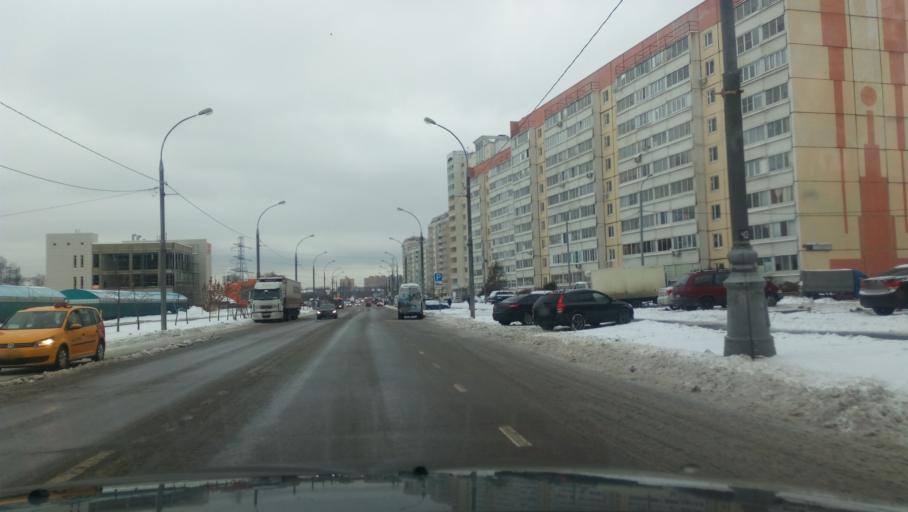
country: RU
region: Moscow
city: Nekrasovka
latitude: 55.7147
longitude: 37.8990
